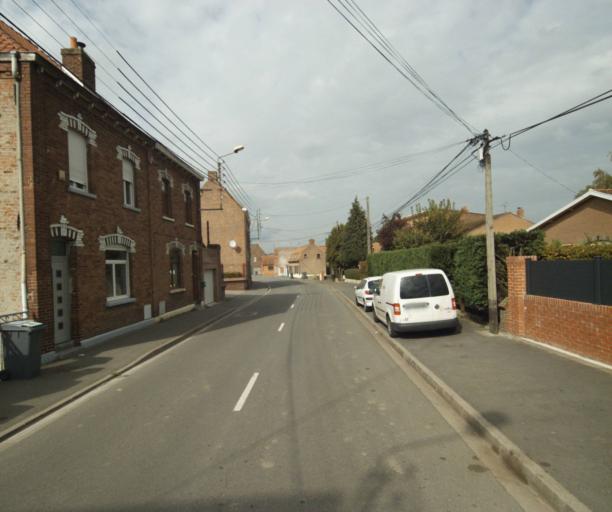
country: FR
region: Nord-Pas-de-Calais
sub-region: Departement du Nord
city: Salome
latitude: 50.5376
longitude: 2.8400
